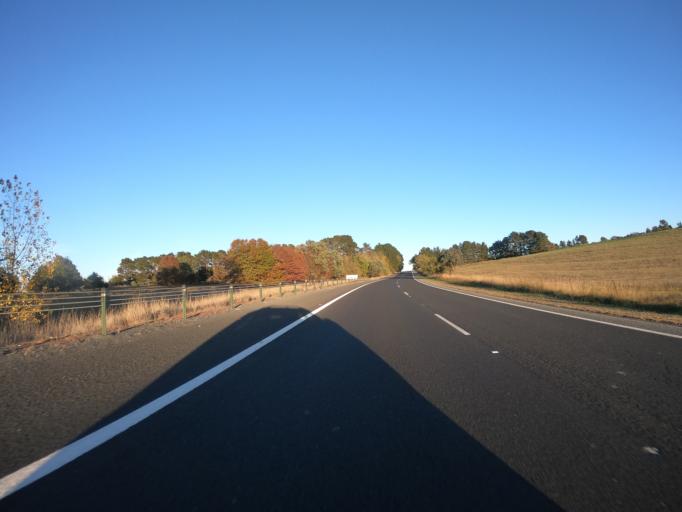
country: AU
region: New South Wales
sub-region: Goulburn Mulwaree
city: Goulburn
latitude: -34.8928
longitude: 149.5235
